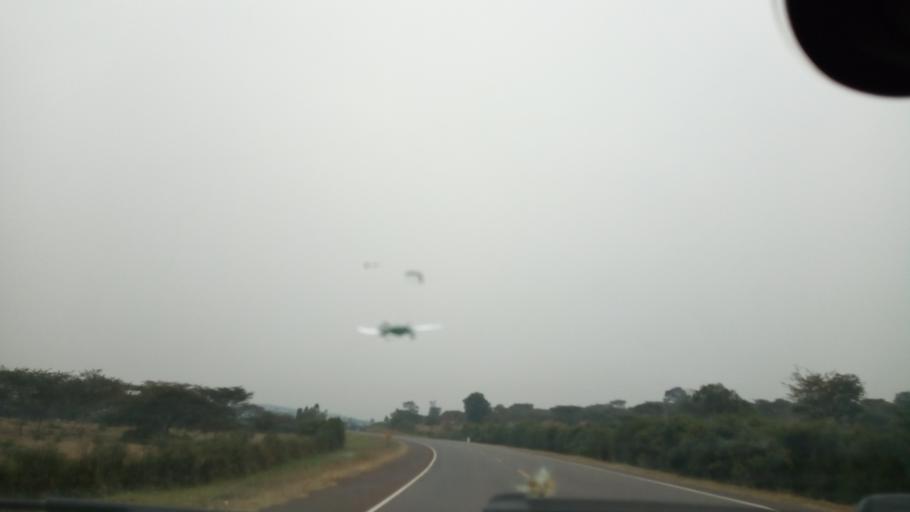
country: UG
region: Western Region
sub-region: Mbarara District
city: Mbarara
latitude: -0.7122
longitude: 30.7154
